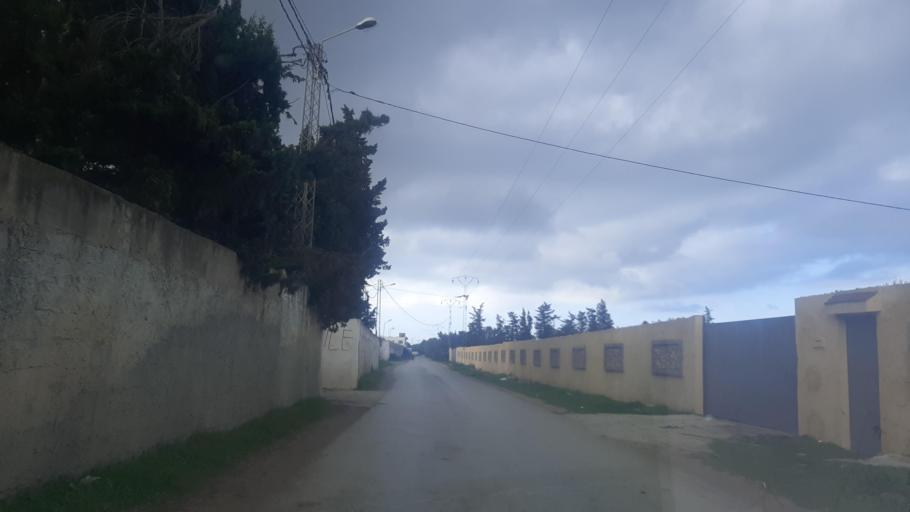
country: TN
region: Nabul
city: Manzil Bu Zalafah
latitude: 36.7316
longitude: 10.5382
